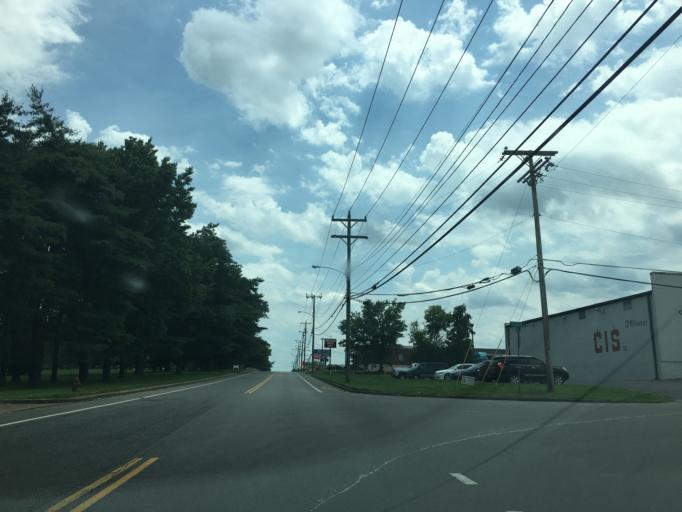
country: US
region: Tennessee
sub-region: Davidson County
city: Nashville
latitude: 36.1325
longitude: -86.7416
